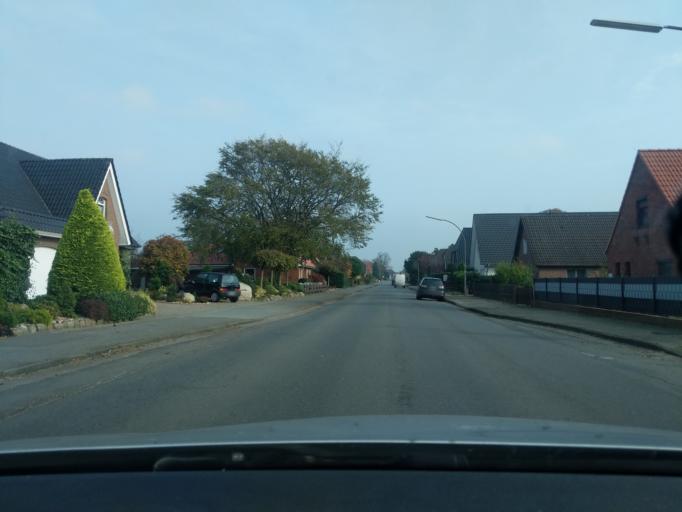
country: DE
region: Lower Saxony
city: Lamstedt
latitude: 53.6370
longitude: 9.0887
